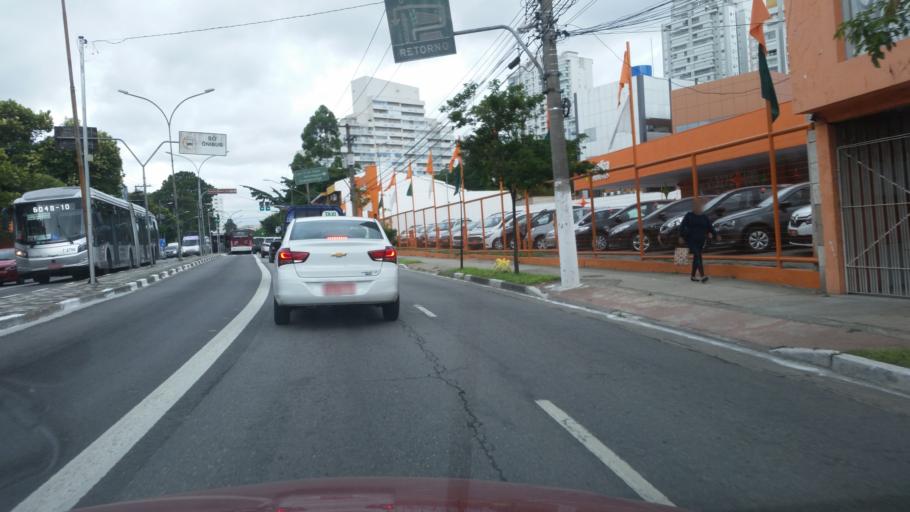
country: BR
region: Sao Paulo
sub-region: Taboao Da Serra
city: Taboao da Serra
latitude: -23.6465
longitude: -46.7057
